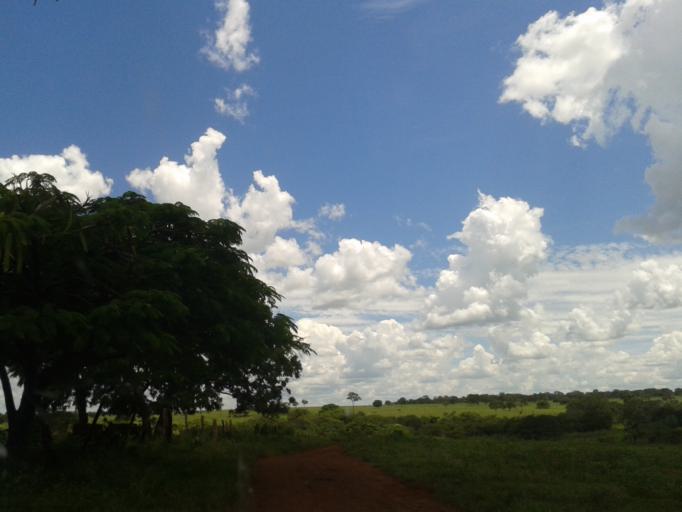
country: BR
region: Minas Gerais
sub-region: Capinopolis
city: Capinopolis
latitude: -18.7850
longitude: -49.8007
